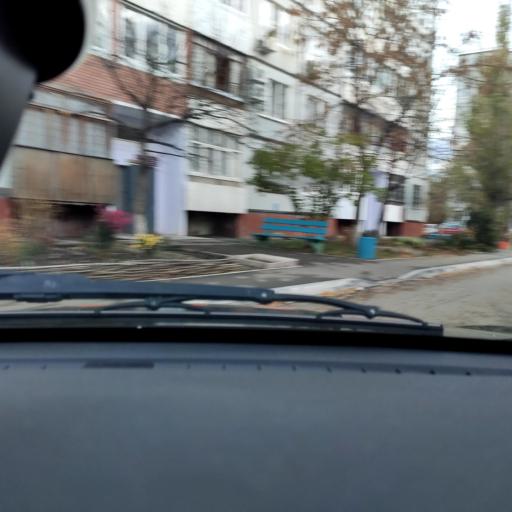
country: RU
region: Samara
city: Tol'yatti
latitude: 53.5078
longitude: 49.4412
